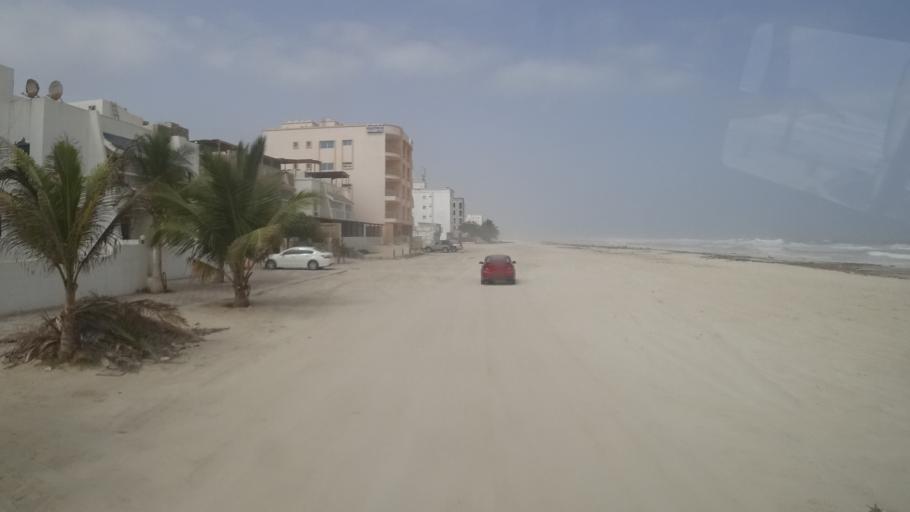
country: OM
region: Zufar
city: Salalah
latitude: 17.0088
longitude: 54.1583
